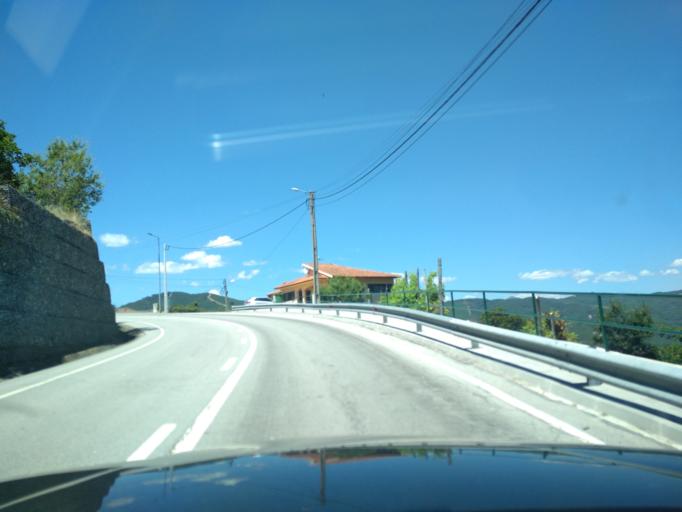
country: PT
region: Vila Real
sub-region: Ribeira de Pena
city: Sobreira
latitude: 41.5261
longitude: -7.7894
